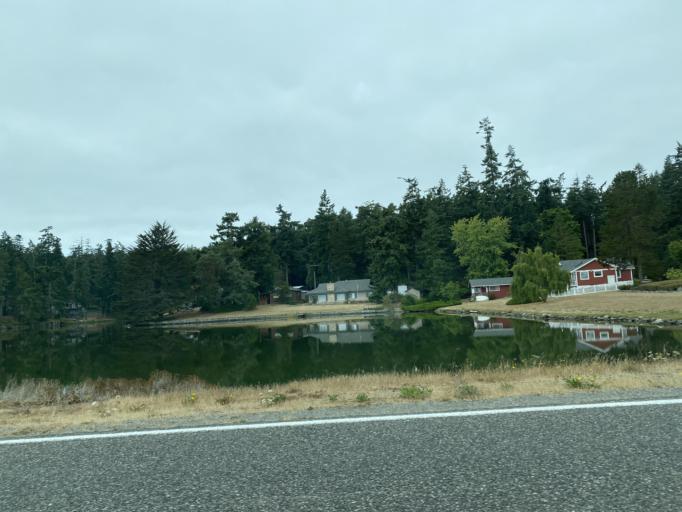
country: US
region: Washington
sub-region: Island County
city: Coupeville
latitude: 48.2281
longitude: -122.7346
